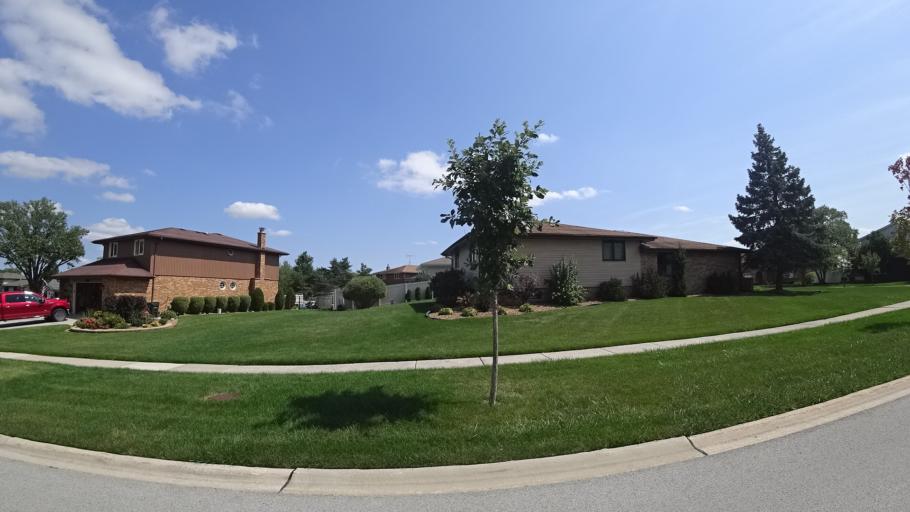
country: US
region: Illinois
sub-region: Cook County
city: Orland Hills
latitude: 41.5667
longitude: -87.8400
